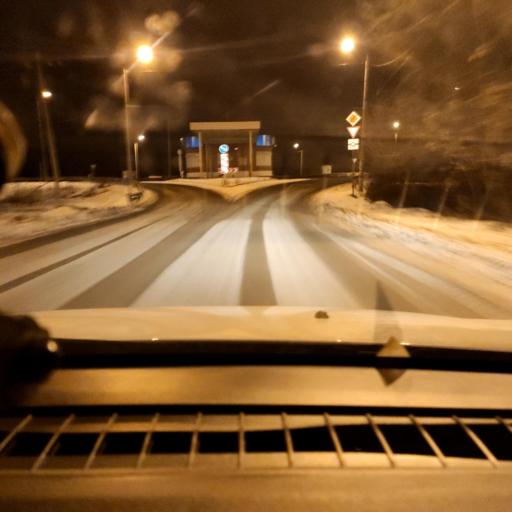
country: RU
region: Samara
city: Novokuybyshevsk
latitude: 53.1432
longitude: 49.9854
